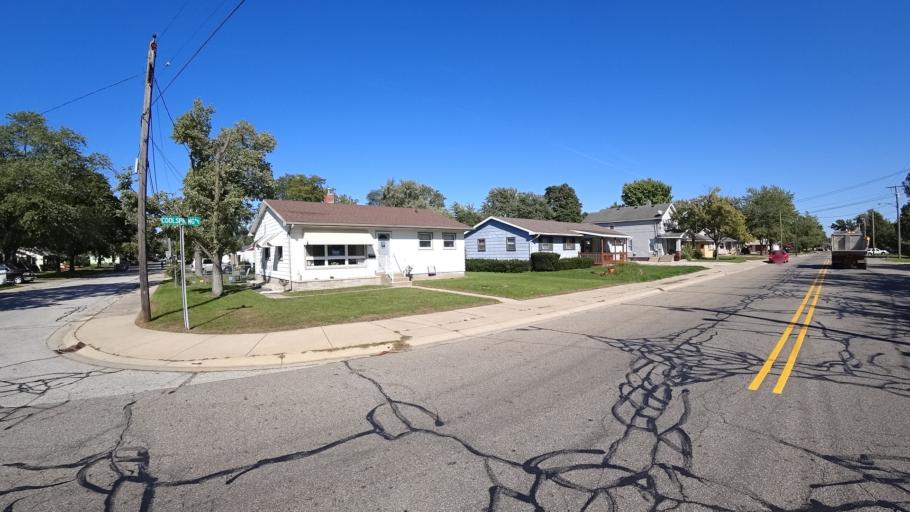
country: US
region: Indiana
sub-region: LaPorte County
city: Michigan City
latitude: 41.6948
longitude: -86.8989
